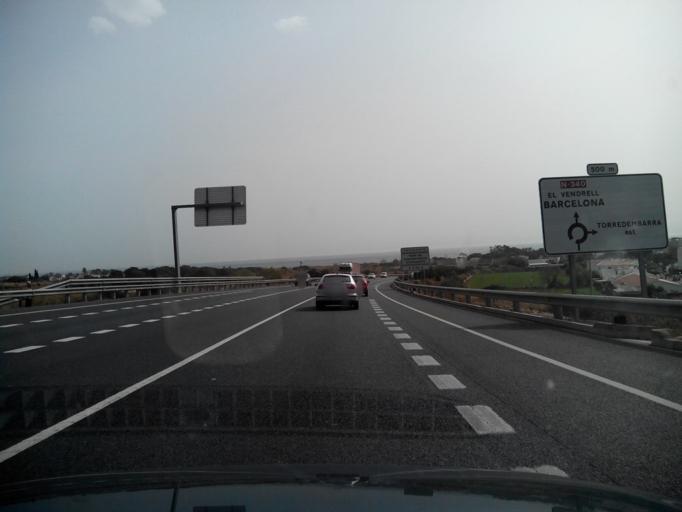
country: ES
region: Catalonia
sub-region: Provincia de Tarragona
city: Creixell
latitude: 41.1592
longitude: 1.4210
